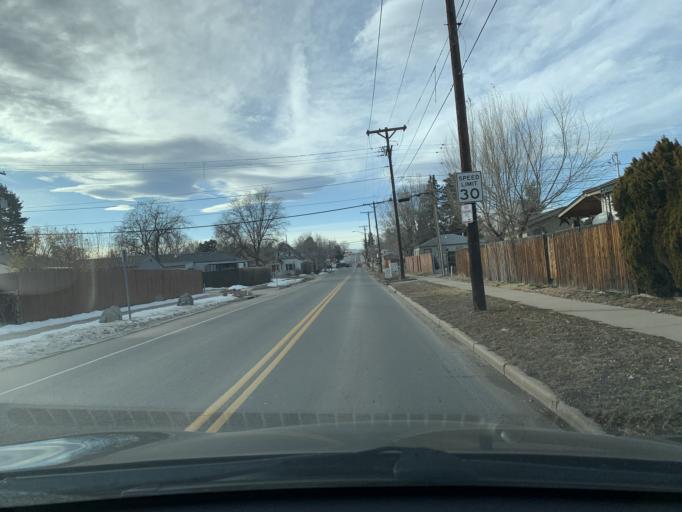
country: US
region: Colorado
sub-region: Jefferson County
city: Edgewater
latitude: 39.7330
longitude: -105.0299
